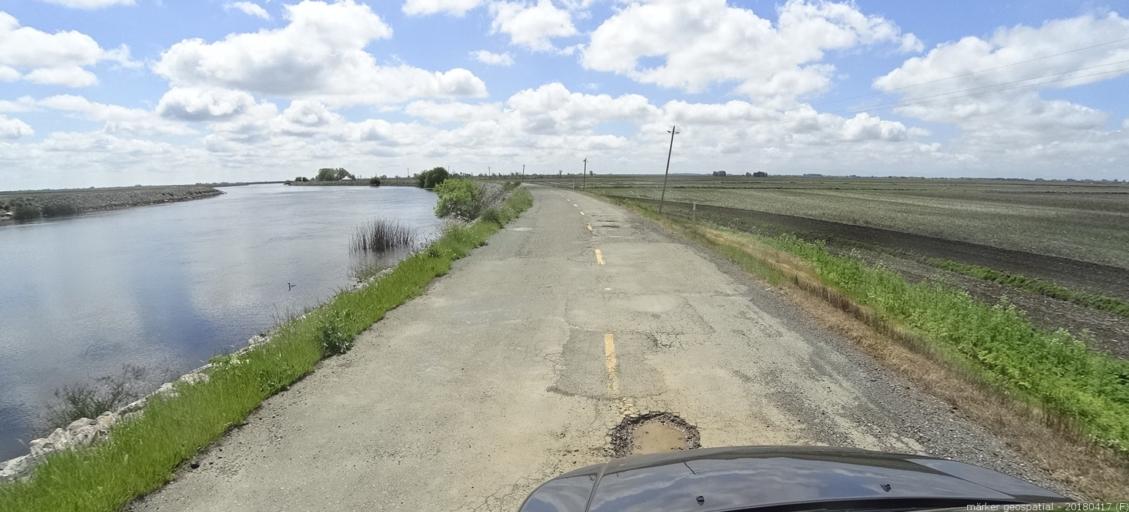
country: US
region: California
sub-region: Sacramento County
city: Walnut Grove
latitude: 38.1949
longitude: -121.5297
